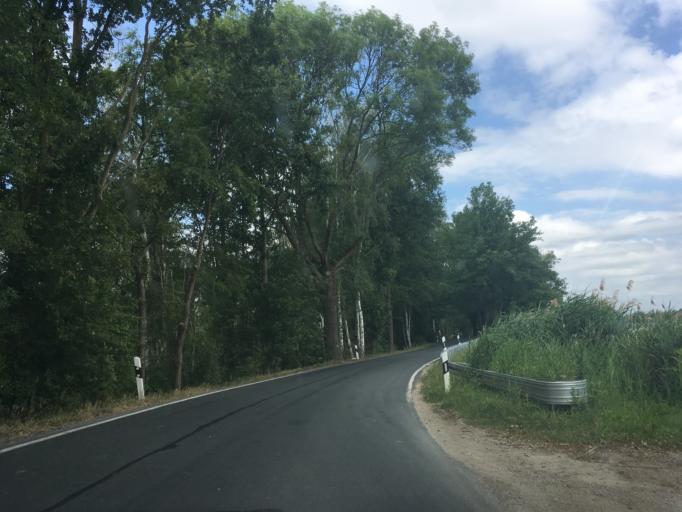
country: DE
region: Saxony
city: Tauscha
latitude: 51.2387
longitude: 13.7886
